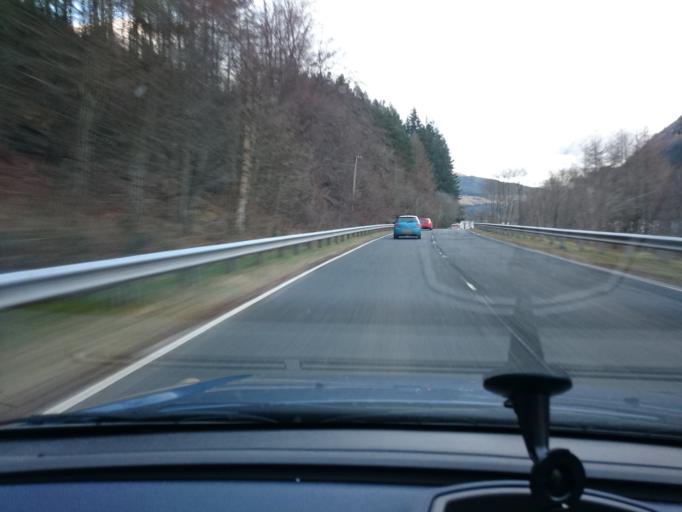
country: GB
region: Scotland
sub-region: Stirling
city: Callander
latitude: 56.2988
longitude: -4.3052
